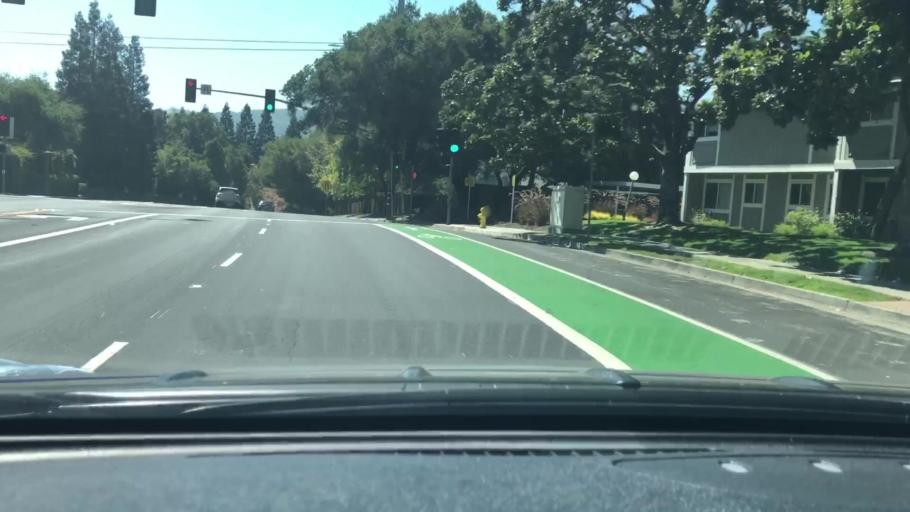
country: US
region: California
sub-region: Santa Clara County
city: Los Gatos
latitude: 37.2357
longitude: -121.9680
